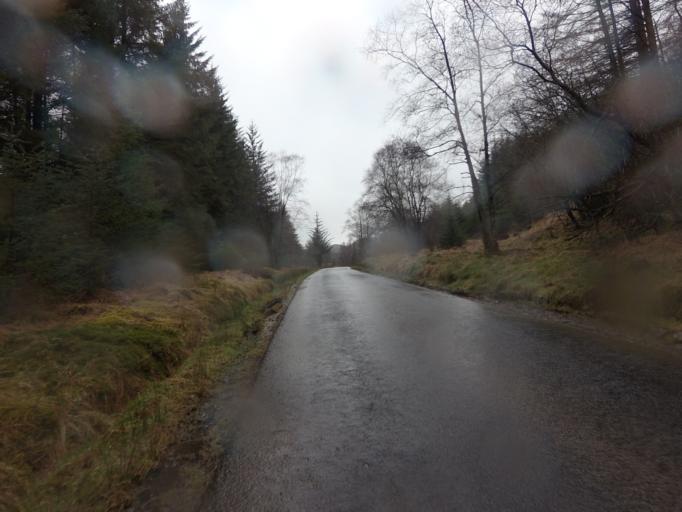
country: GB
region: Scotland
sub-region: West Dunbartonshire
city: Balloch
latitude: 56.2321
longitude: -4.5588
